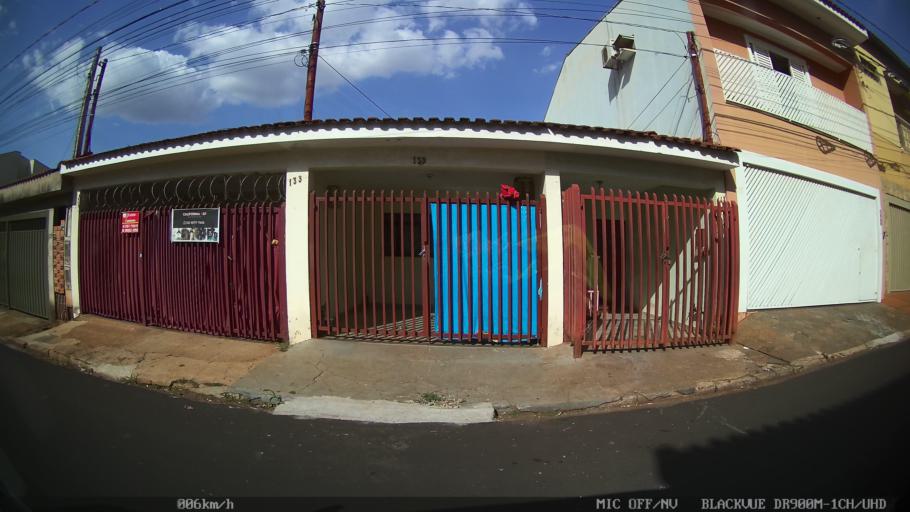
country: BR
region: Sao Paulo
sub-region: Ribeirao Preto
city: Ribeirao Preto
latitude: -21.1810
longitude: -47.8274
